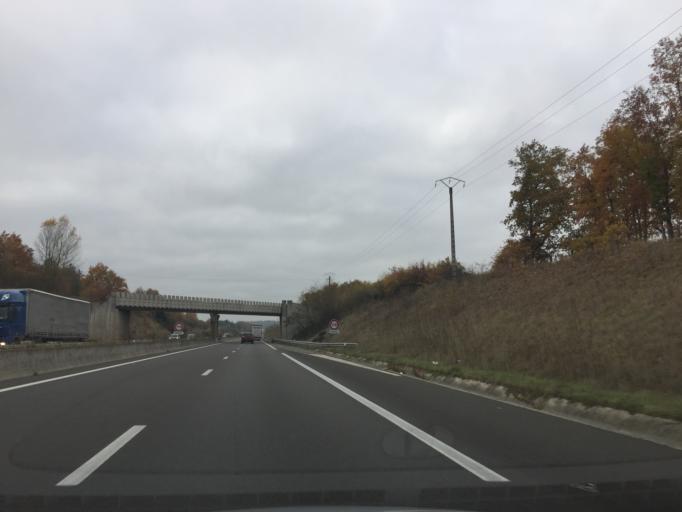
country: FR
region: Auvergne
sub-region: Departement de l'Allier
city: Domerat
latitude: 46.3543
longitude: 2.5461
